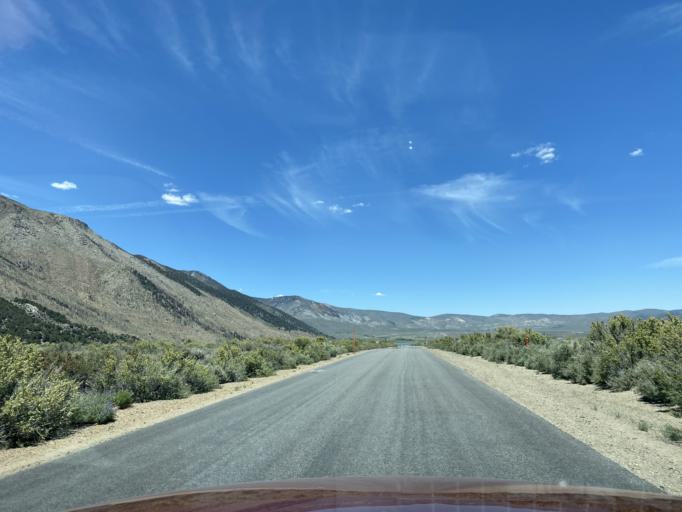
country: US
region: California
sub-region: Mono County
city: Bridgeport
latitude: 37.9631
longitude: -119.1210
